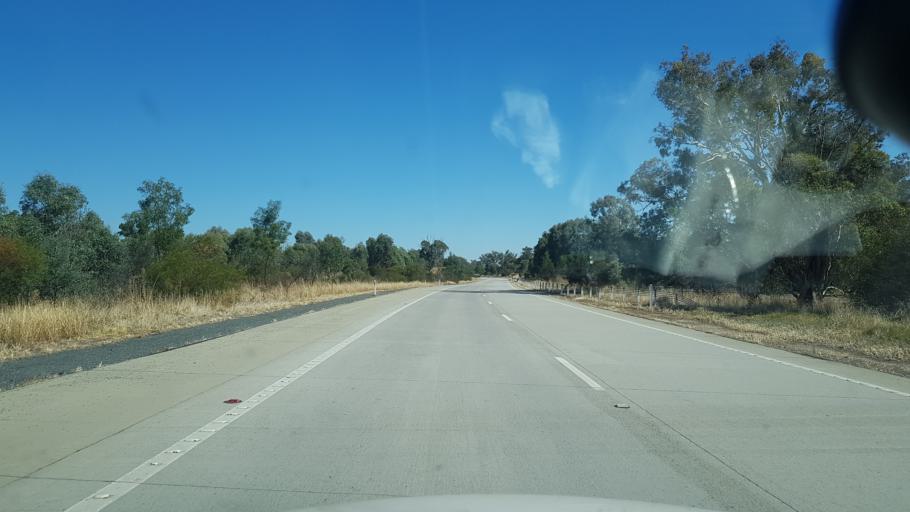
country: AU
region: New South Wales
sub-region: Greater Hume Shire
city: Holbrook
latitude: -35.8918
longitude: 147.1716
